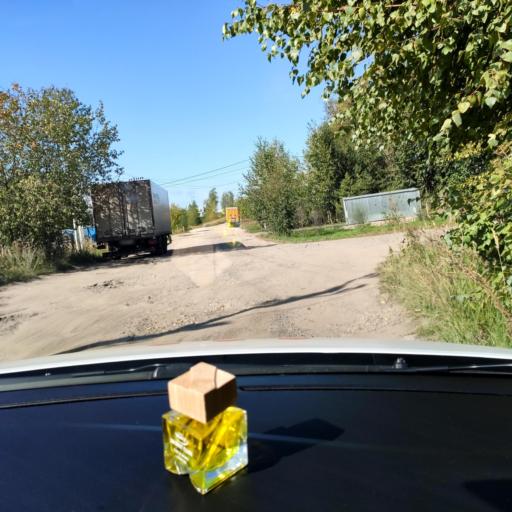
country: RU
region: Tatarstan
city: Vysokaya Gora
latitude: 55.8797
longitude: 49.2479
